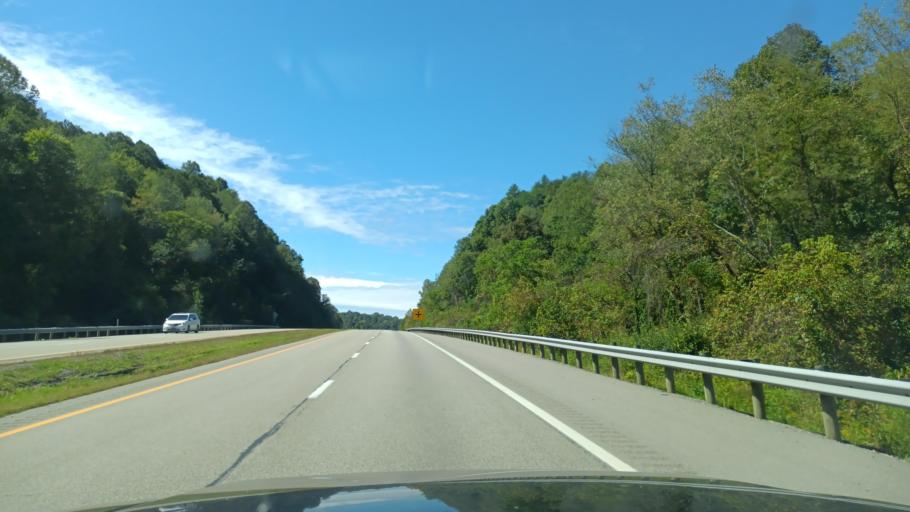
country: US
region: West Virginia
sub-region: Harrison County
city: Salem
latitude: 39.2943
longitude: -80.5563
